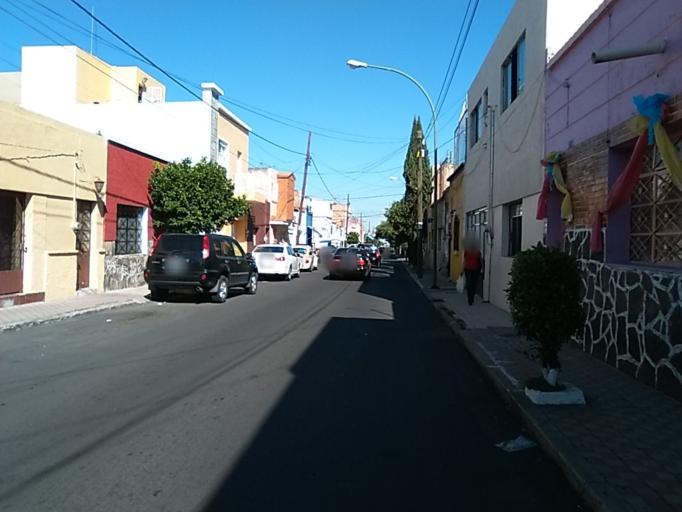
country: MX
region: Jalisco
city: Guadalajara
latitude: 20.6855
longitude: -103.3643
